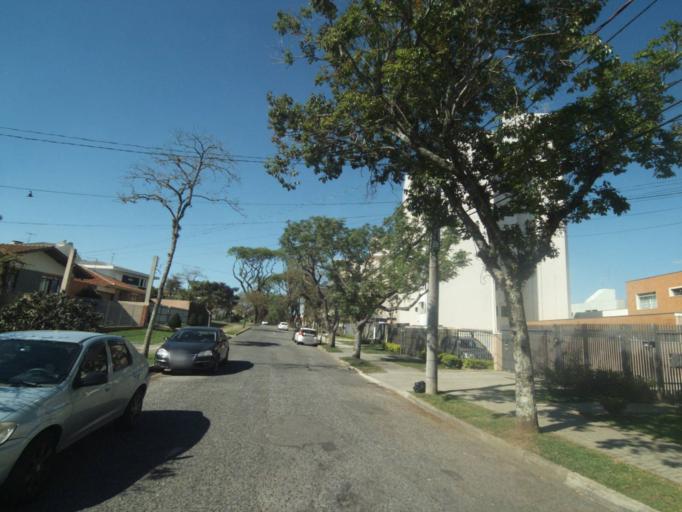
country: BR
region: Parana
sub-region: Curitiba
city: Curitiba
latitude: -25.3972
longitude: -49.2412
